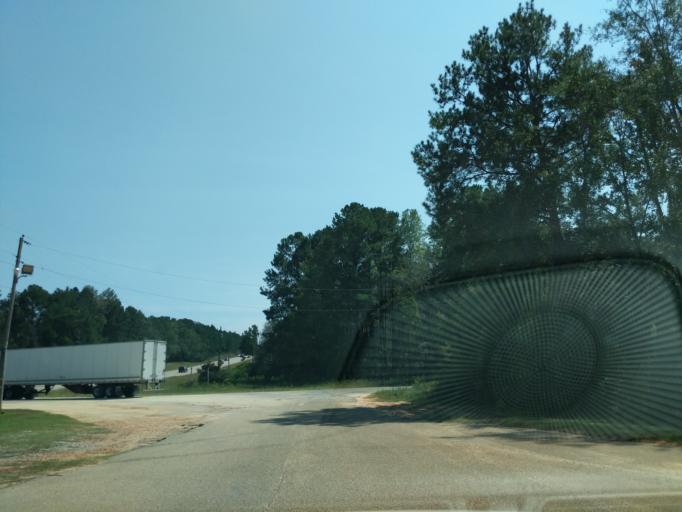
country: US
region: Alabama
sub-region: Butler County
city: Georgiana
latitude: 31.4875
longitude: -86.6828
